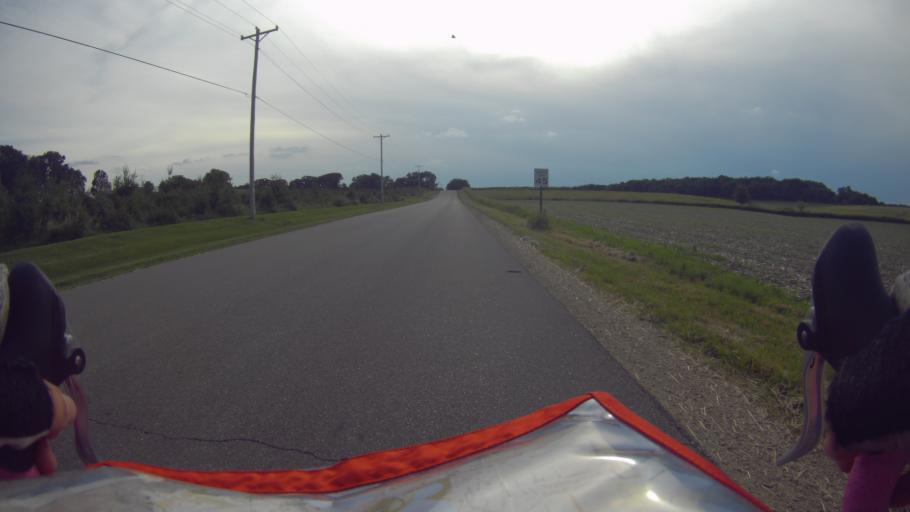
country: US
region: Wisconsin
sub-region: Dane County
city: McFarland
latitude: 43.0043
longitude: -89.3476
